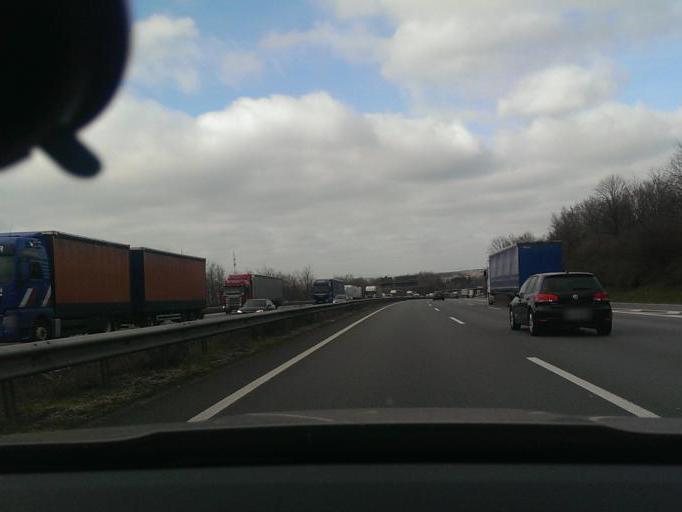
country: DE
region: North Rhine-Westphalia
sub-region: Regierungsbezirk Detmold
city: Oerlinghausen
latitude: 51.9987
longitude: 8.6200
